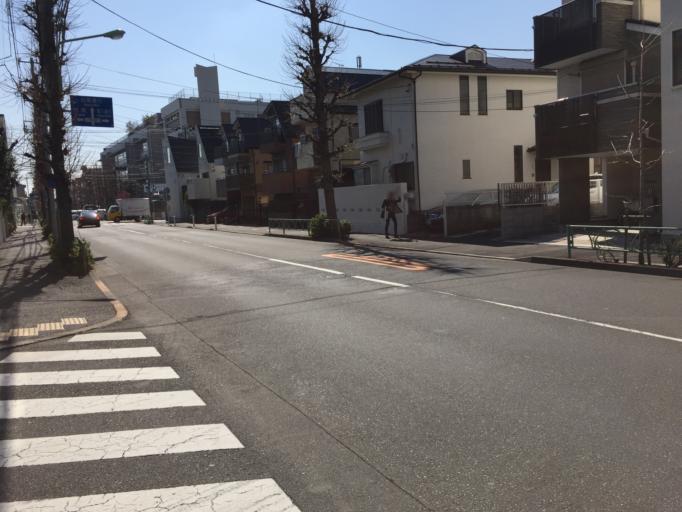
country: JP
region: Tokyo
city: Tokyo
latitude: 35.6149
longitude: 139.6529
